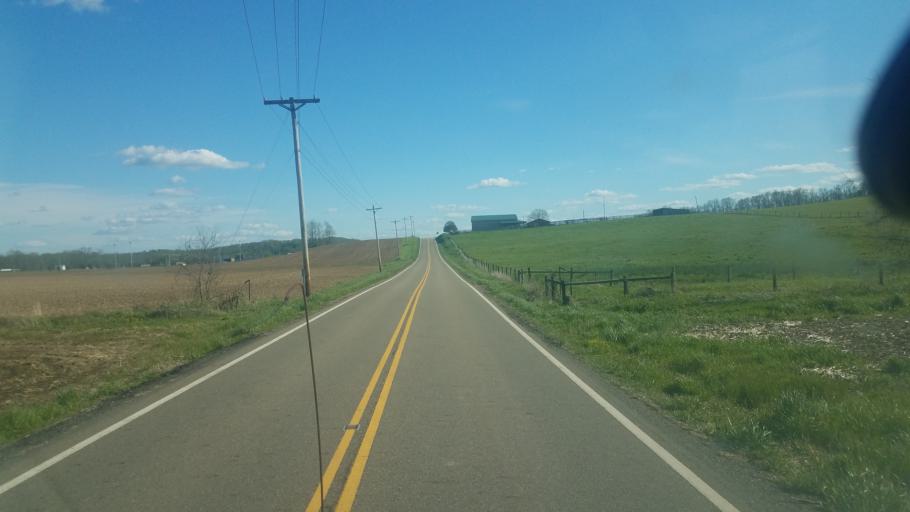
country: US
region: Ohio
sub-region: Coshocton County
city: Coshocton
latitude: 40.3478
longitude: -81.9593
